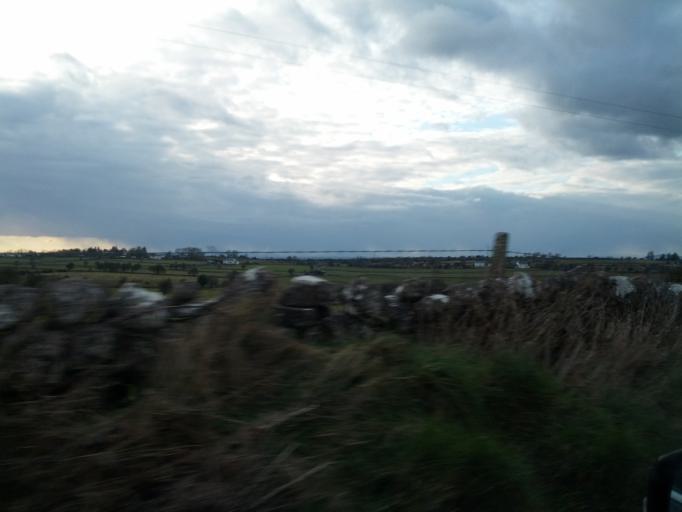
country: IE
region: Connaught
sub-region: County Galway
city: Athenry
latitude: 53.3944
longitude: -8.7460
